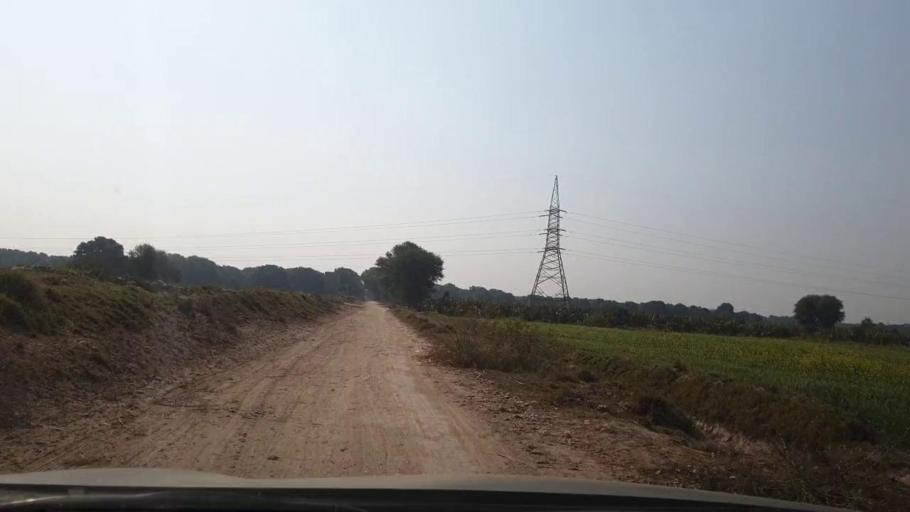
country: PK
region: Sindh
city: Tando Allahyar
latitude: 25.5000
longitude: 68.7860
